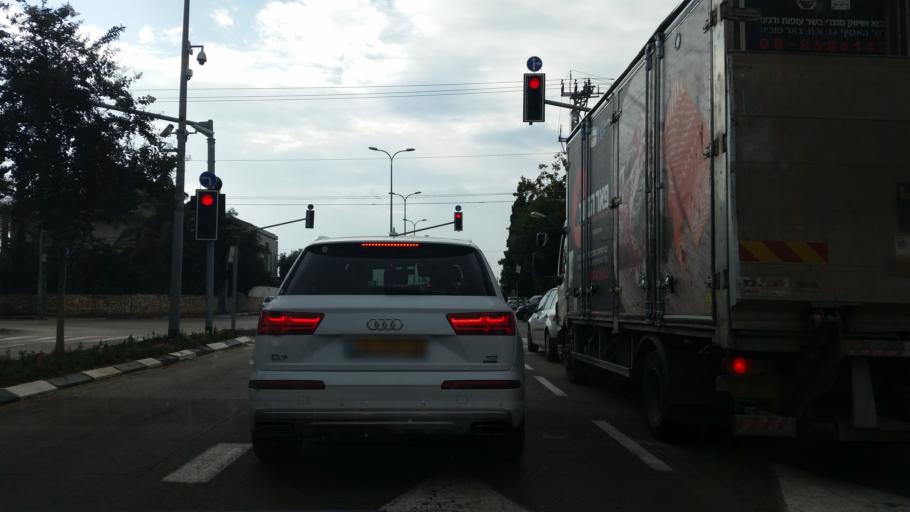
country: IL
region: Central District
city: Ra'anana
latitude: 32.1751
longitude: 34.8691
